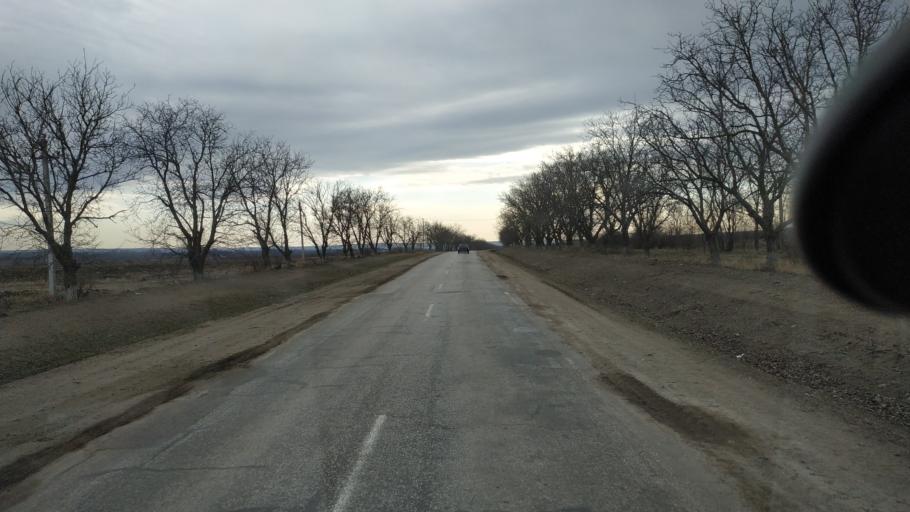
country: MD
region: Criuleni
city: Criuleni
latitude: 47.1968
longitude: 29.1509
